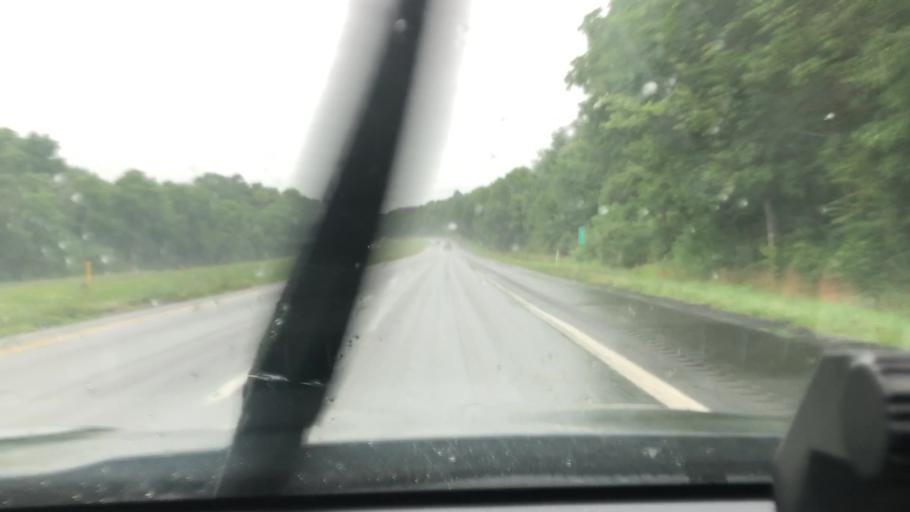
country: US
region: Pennsylvania
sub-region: Northampton County
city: Wind Gap
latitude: 40.8178
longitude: -75.2988
